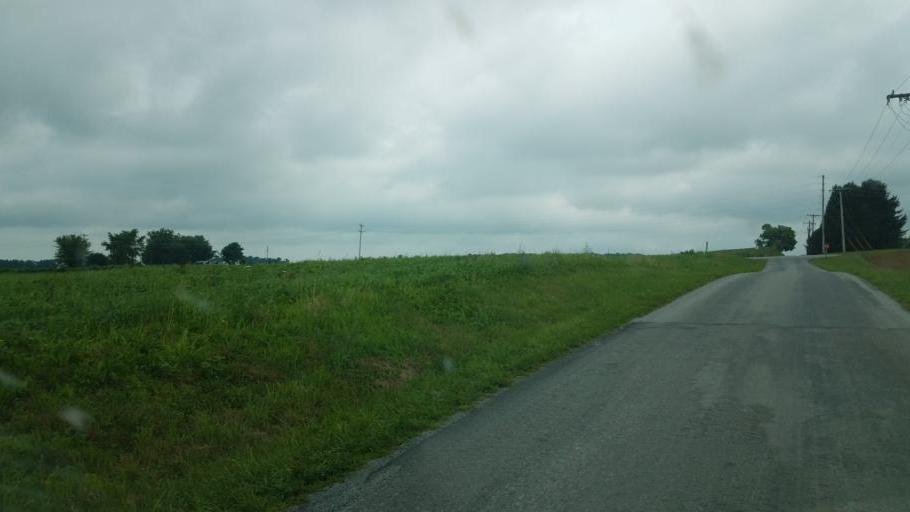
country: US
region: Ohio
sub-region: Highland County
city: Leesburg
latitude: 39.2384
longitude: -83.4674
